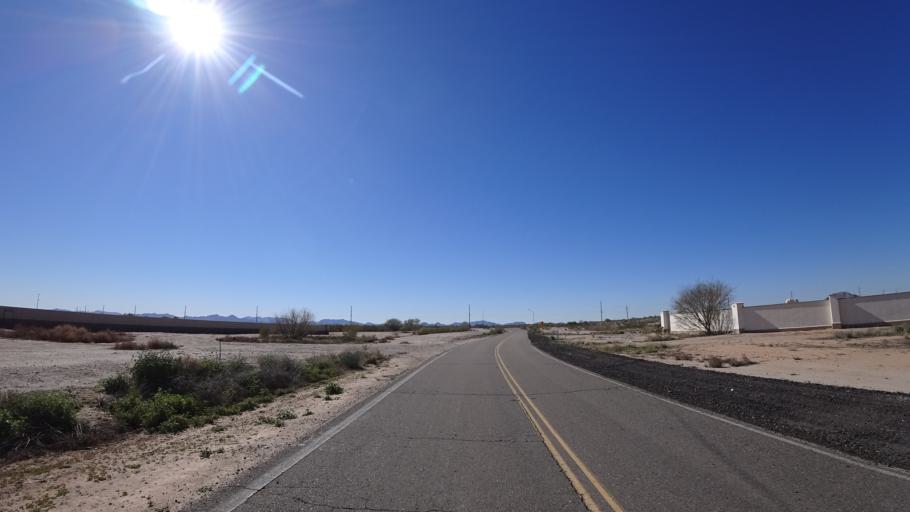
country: US
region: Arizona
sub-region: Maricopa County
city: Buckeye
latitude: 33.2931
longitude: -112.4464
